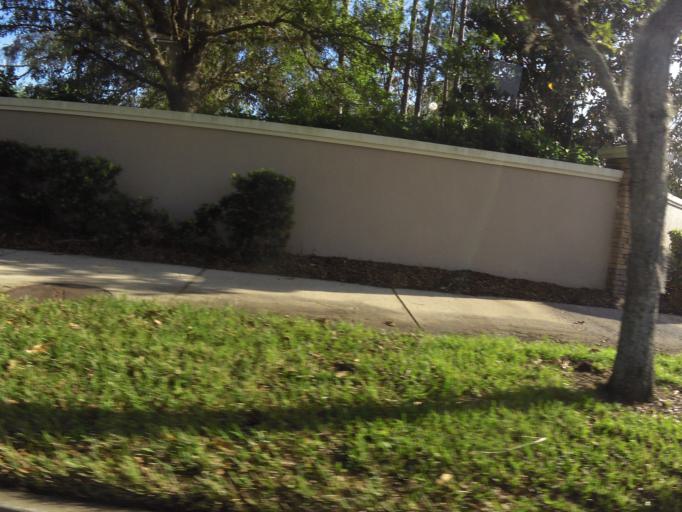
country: US
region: Florida
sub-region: Saint Johns County
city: Villano Beach
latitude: 29.9933
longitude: -81.4717
